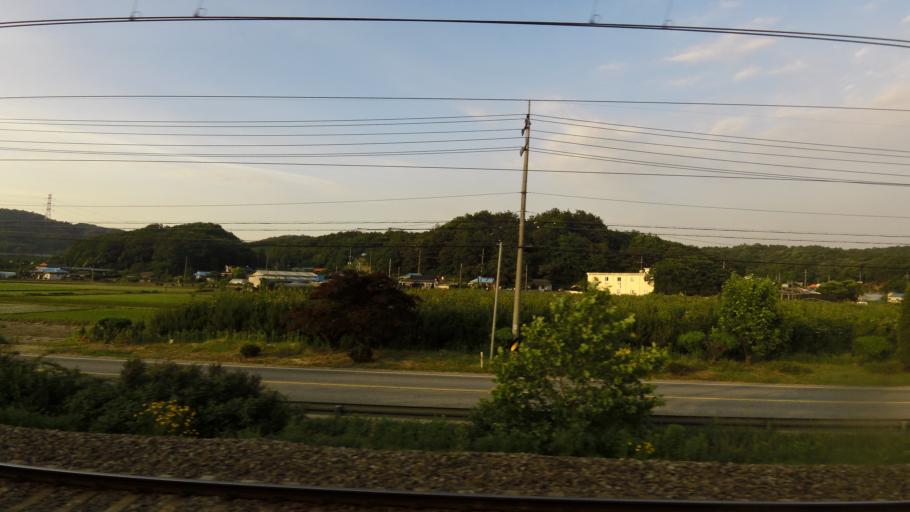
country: KR
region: Chungcheongnam-do
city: Cheonan
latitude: 36.6627
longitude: 127.2561
